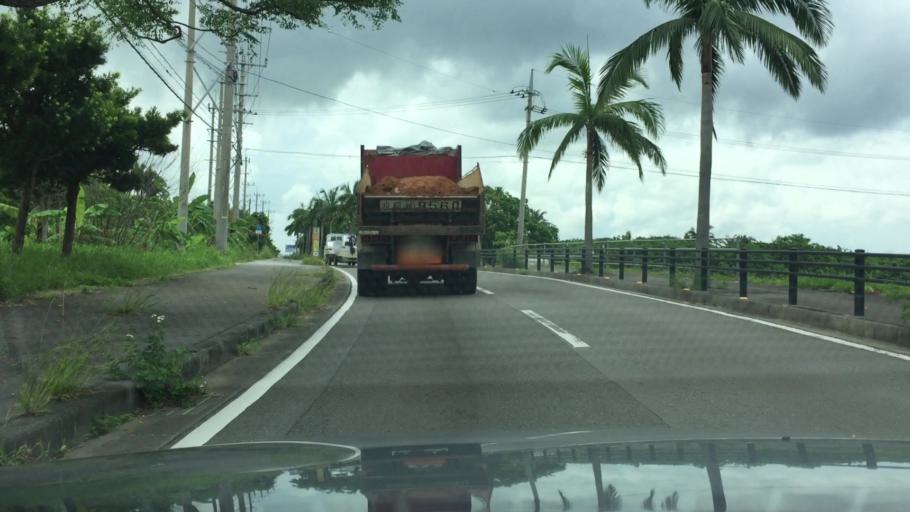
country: JP
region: Okinawa
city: Ishigaki
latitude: 24.4541
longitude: 124.1979
